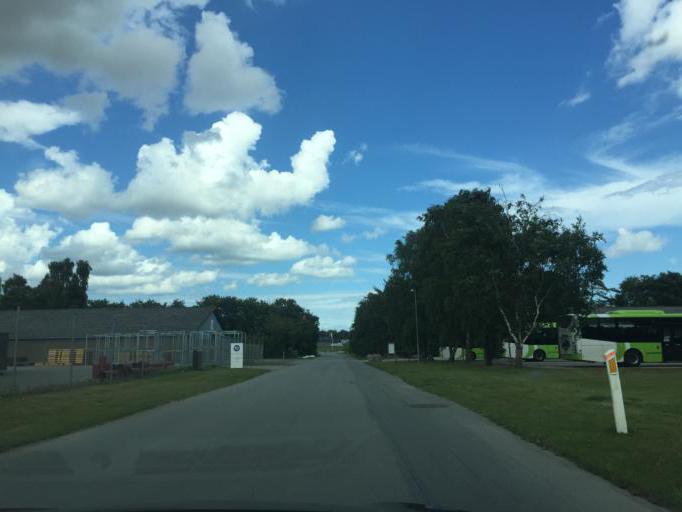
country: DK
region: South Denmark
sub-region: Nordfyns Kommune
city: Otterup
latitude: 55.5060
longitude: 10.3997
